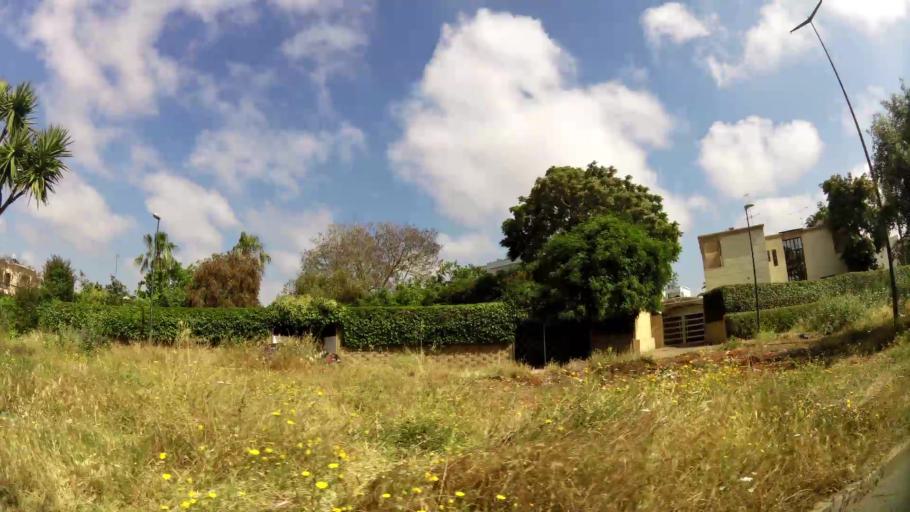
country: MA
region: Rabat-Sale-Zemmour-Zaer
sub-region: Skhirate-Temara
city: Temara
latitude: 33.9656
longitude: -6.8677
